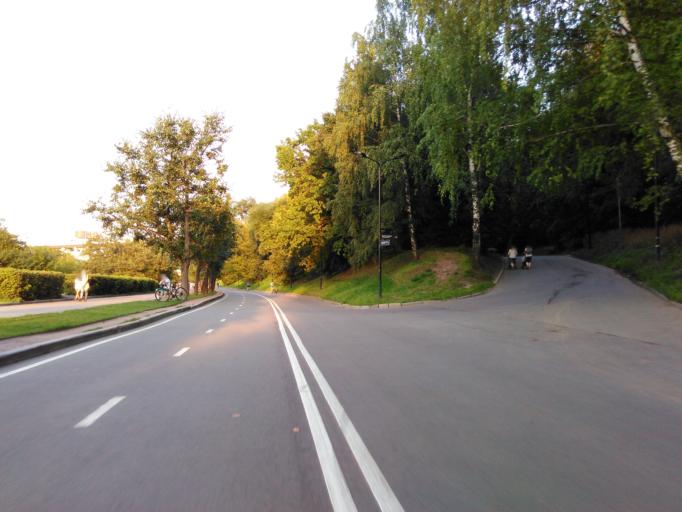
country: RU
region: Moscow
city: Luzhniki
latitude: 55.7099
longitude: 37.5517
